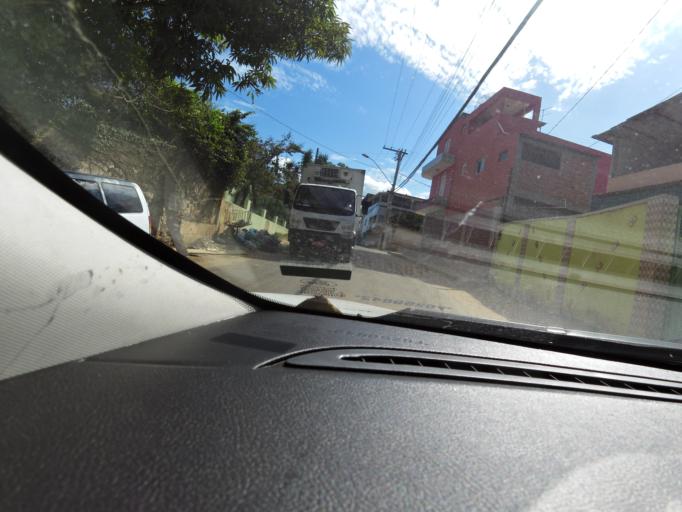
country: BR
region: Espirito Santo
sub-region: Guarapari
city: Guarapari
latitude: -20.6610
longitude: -40.5170
